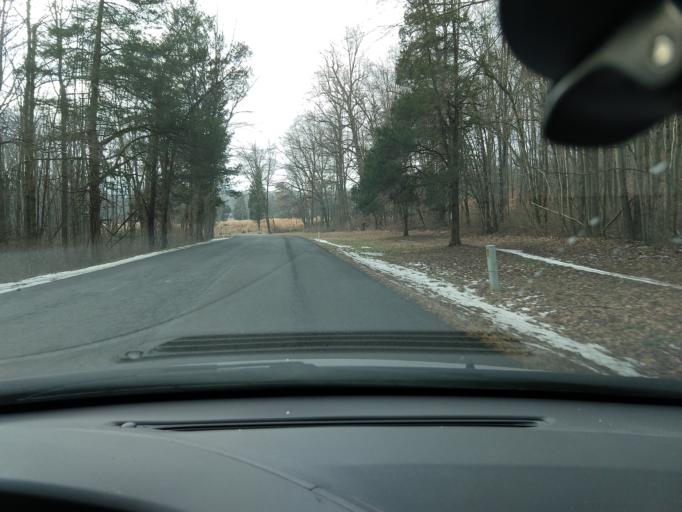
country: US
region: Pennsylvania
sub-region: Chester County
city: Elverson
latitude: 40.2019
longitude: -75.7911
